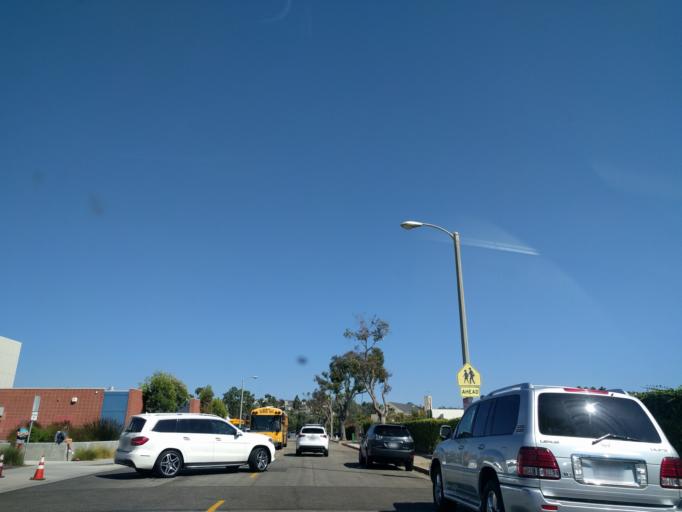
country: US
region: California
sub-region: Orange County
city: Costa Mesa
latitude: 33.6324
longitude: -117.8790
